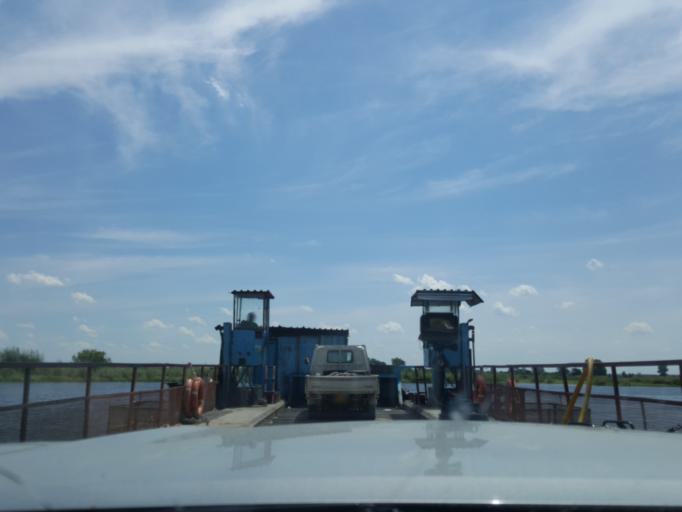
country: BW
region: North West
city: Shakawe
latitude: -18.2764
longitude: 21.7878
